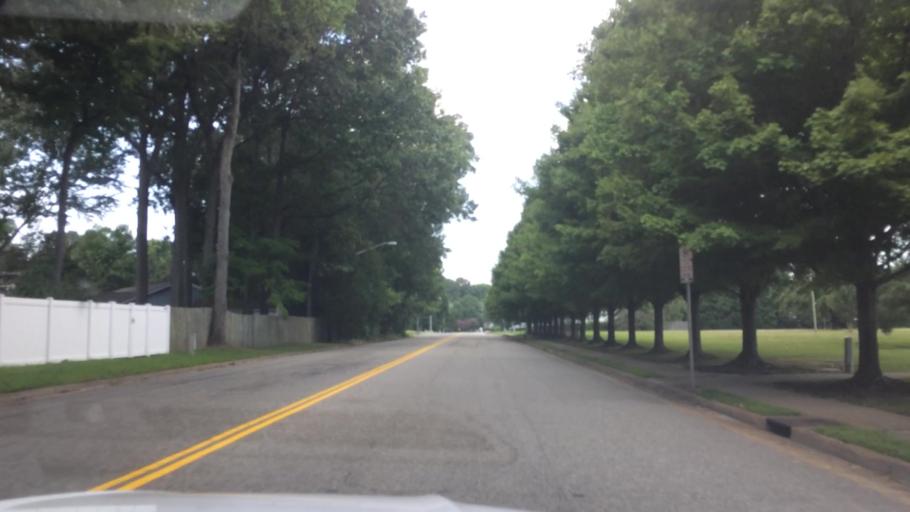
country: US
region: Virginia
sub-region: Isle of Wight County
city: Rushmere
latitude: 37.0934
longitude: -76.5350
